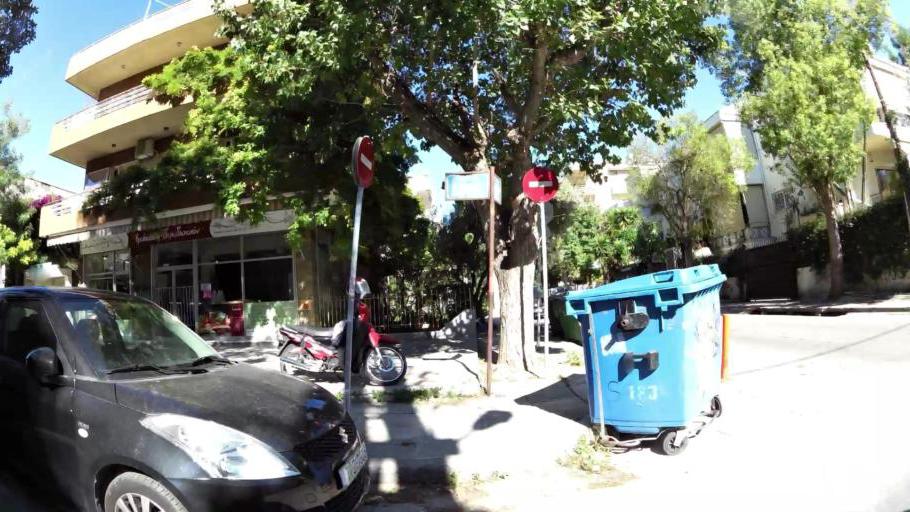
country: GR
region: Attica
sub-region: Nomarchia Athinas
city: Vrilissia
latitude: 38.0272
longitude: 23.8166
